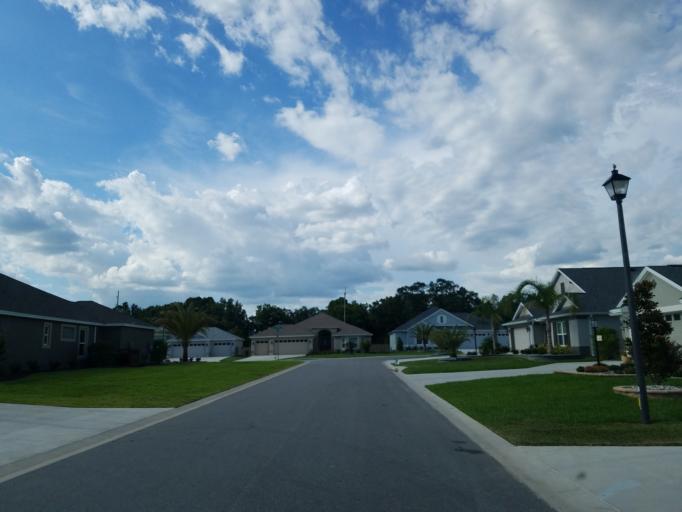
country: US
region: Florida
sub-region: Sumter County
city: Wildwood
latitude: 28.7985
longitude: -82.0360
